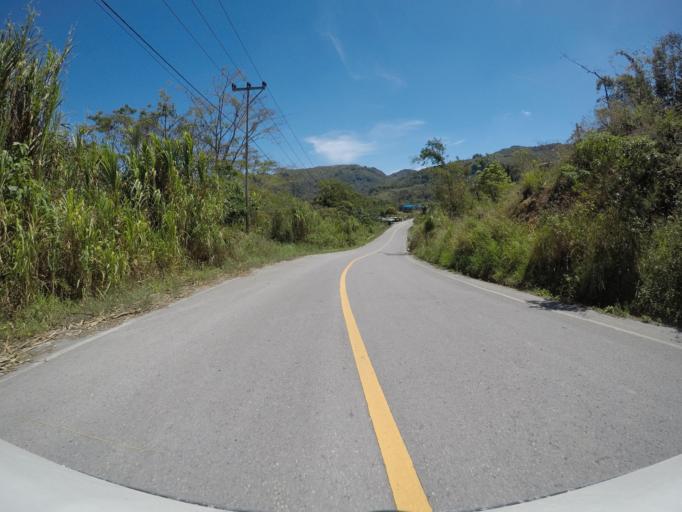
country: TL
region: Manatuto
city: Manatuto
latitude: -8.7814
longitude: 125.9675
